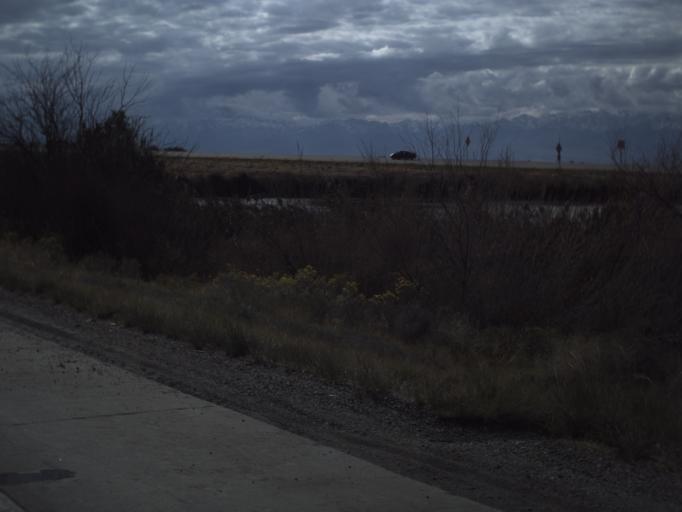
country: US
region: Utah
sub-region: Tooele County
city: Stansbury park
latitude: 40.6961
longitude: -112.2619
